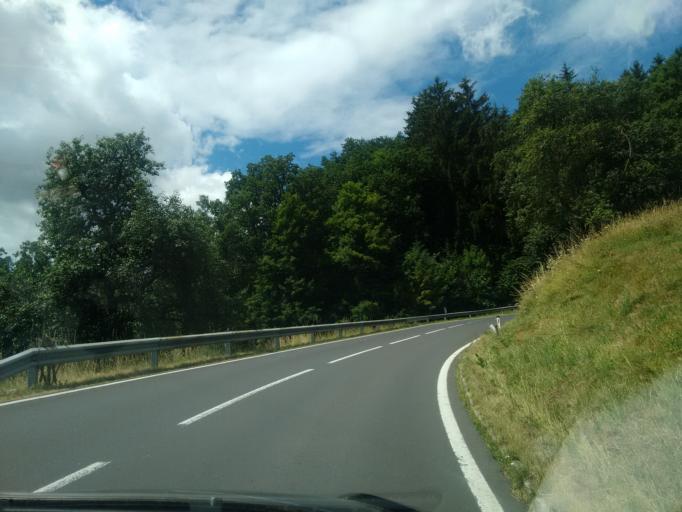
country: AT
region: Upper Austria
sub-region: Politischer Bezirk Urfahr-Umgebung
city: Gramastetten
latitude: 48.3848
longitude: 14.1916
